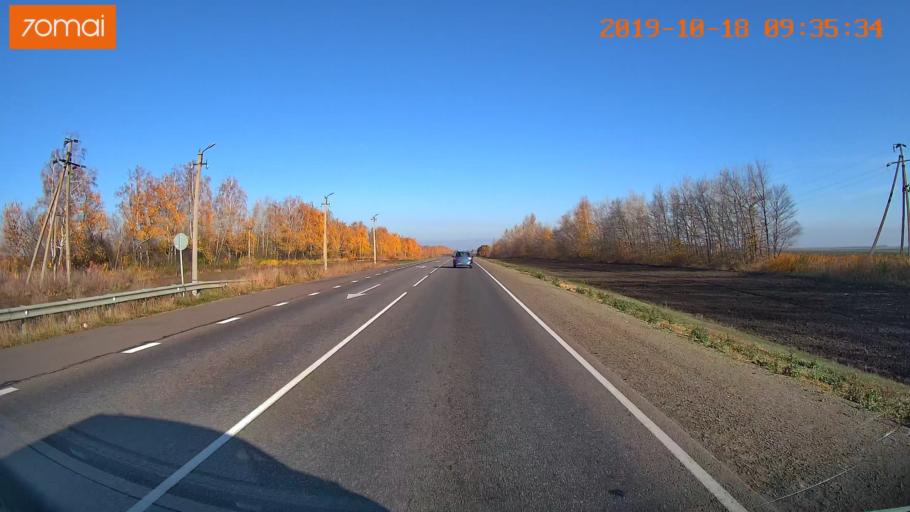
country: RU
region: Tula
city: Yefremov
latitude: 53.1941
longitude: 38.1481
